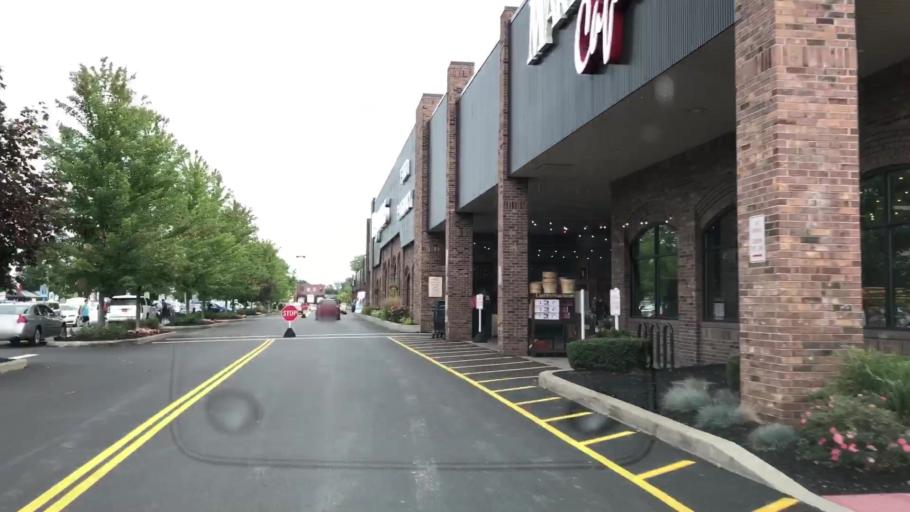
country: US
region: New York
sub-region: Erie County
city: Depew
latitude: 42.8823
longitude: -78.6996
